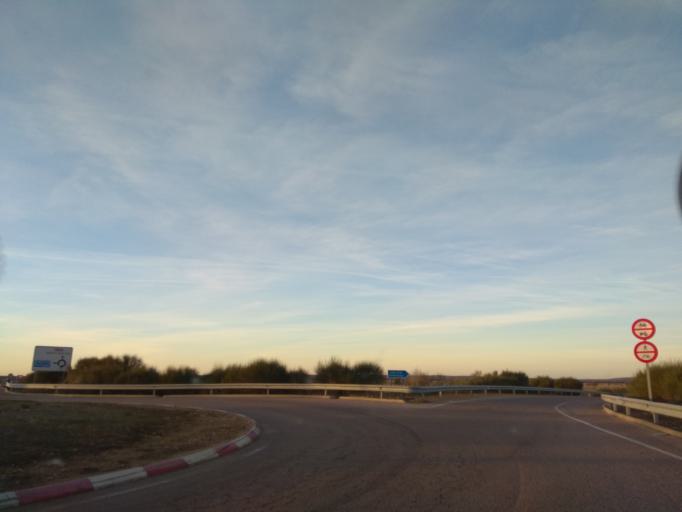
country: ES
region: Castille and Leon
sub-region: Provincia de Salamanca
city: Castraz
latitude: 40.7126
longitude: -6.3887
